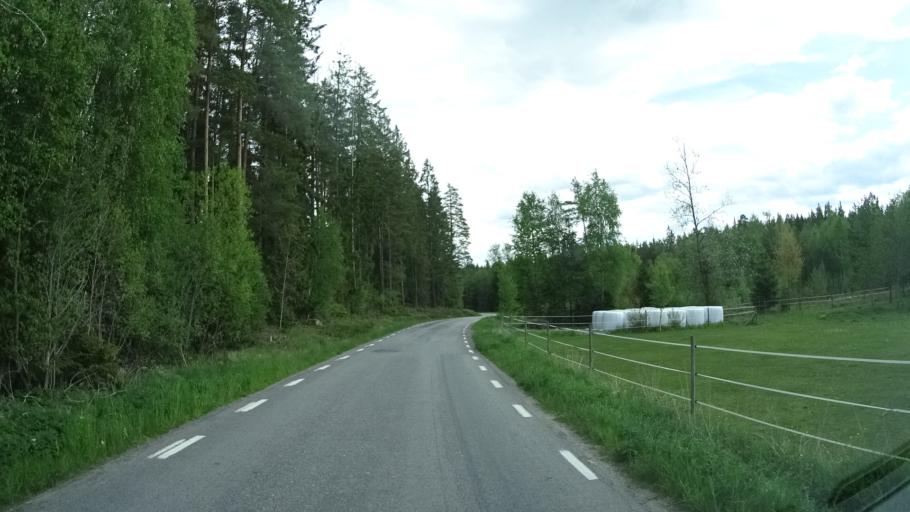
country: SE
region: OEstergoetland
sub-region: Finspangs Kommun
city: Finspang
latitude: 58.6011
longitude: 15.7601
